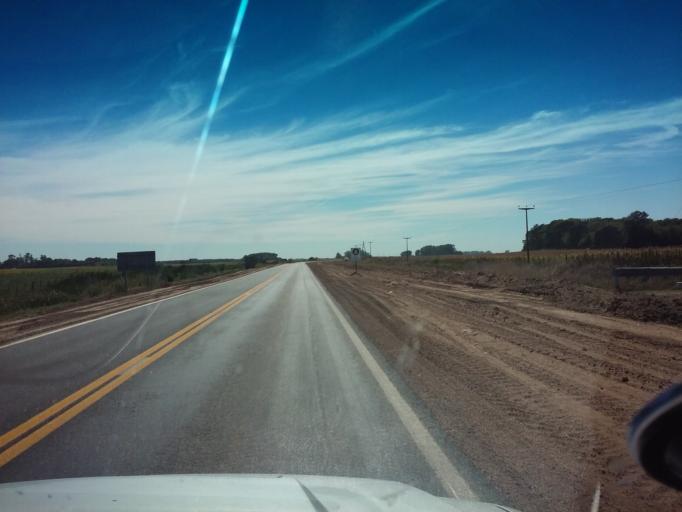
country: AR
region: Buenos Aires
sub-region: Partido de Nueve de Julio
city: Nueve de Julio
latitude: -35.3571
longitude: -60.6991
